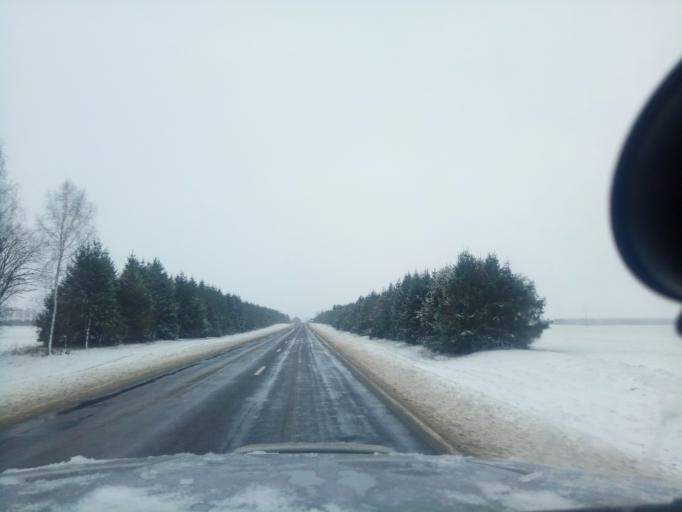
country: BY
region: Minsk
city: Haradzyeya
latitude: 53.3679
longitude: 26.5119
